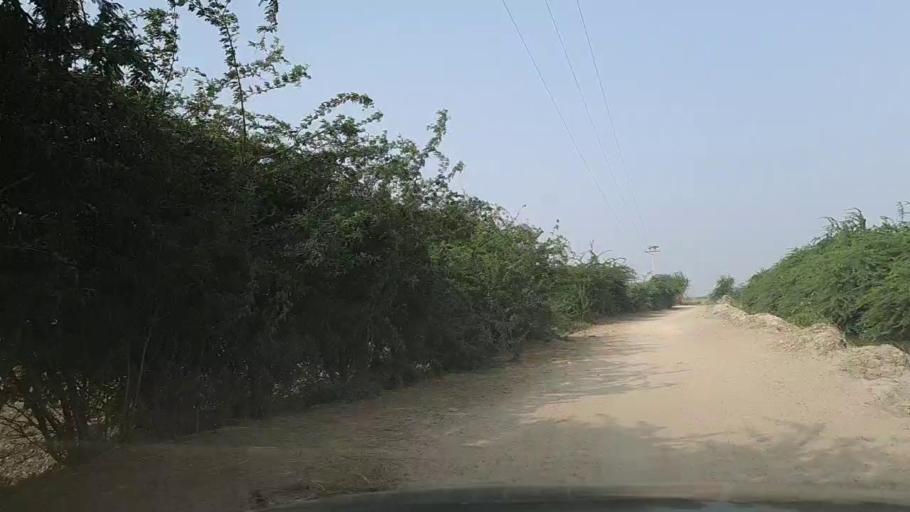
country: PK
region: Sindh
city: Thatta
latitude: 24.7680
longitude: 67.8606
